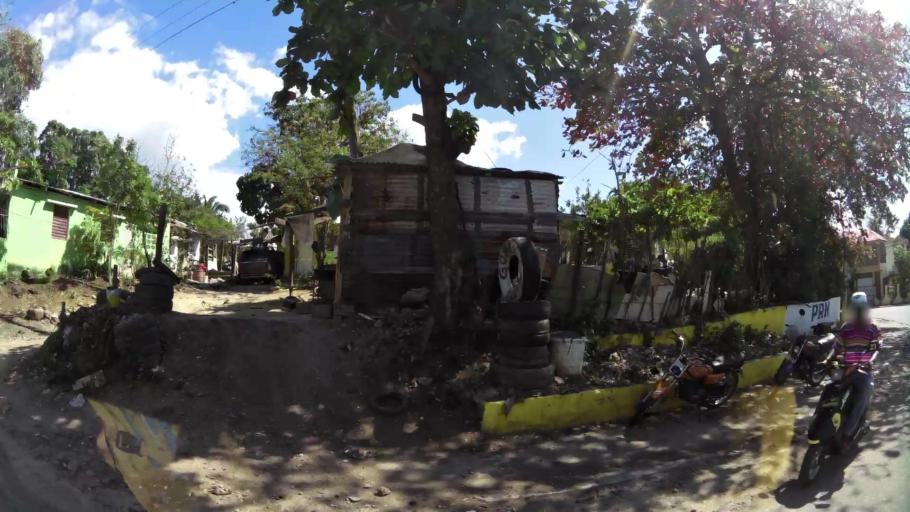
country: DO
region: San Cristobal
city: San Cristobal
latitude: 18.4287
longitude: -70.0849
